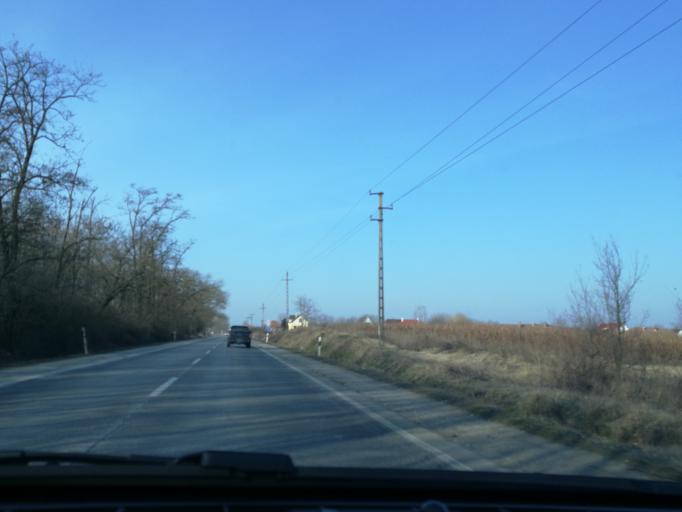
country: HU
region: Szabolcs-Szatmar-Bereg
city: Apagy
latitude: 47.9583
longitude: 21.9517
